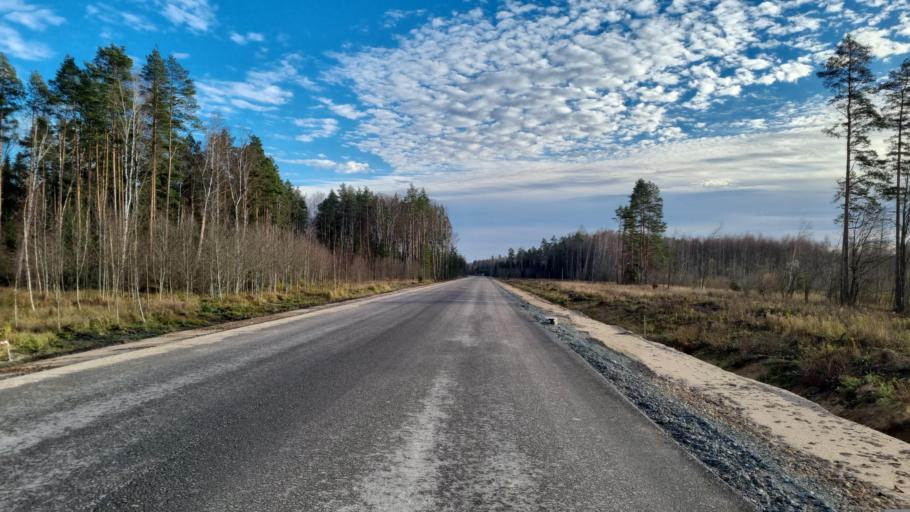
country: LV
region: Kekava
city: Kekava
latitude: 56.8002
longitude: 24.2050
